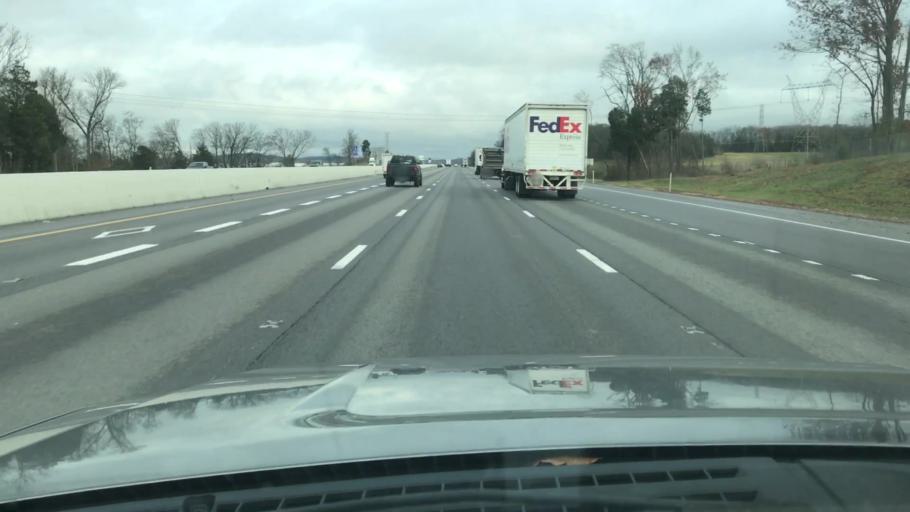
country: US
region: Tennessee
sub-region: Wilson County
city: Rural Hill
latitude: 36.1791
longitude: -86.4504
